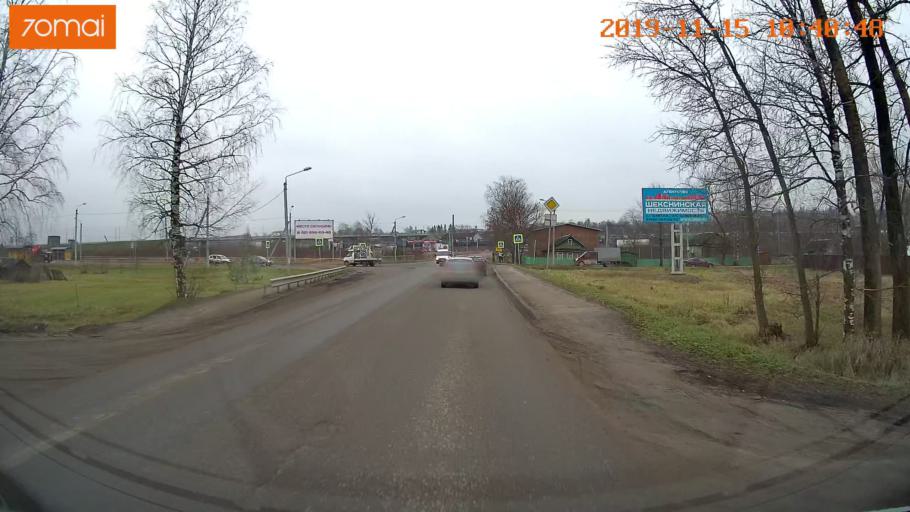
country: RU
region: Vologda
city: Sheksna
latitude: 59.2128
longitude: 38.5098
